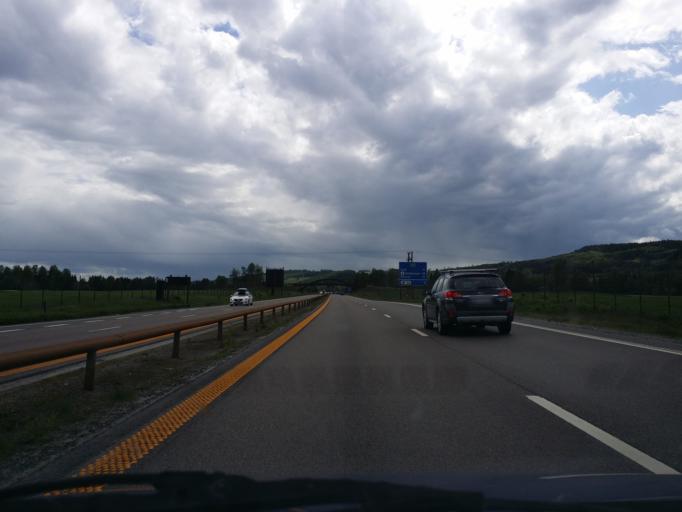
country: NO
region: Akershus
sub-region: Eidsvoll
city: Eidsvoll
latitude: 60.3845
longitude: 11.2116
